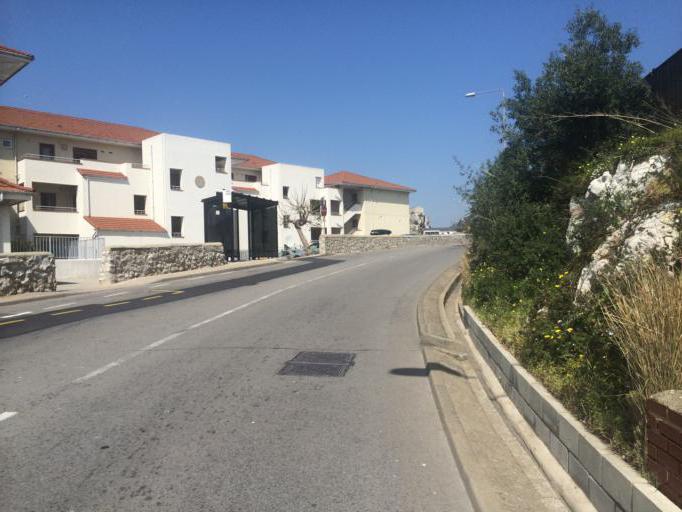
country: GI
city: Gibraltar
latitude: 36.1137
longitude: -5.3487
